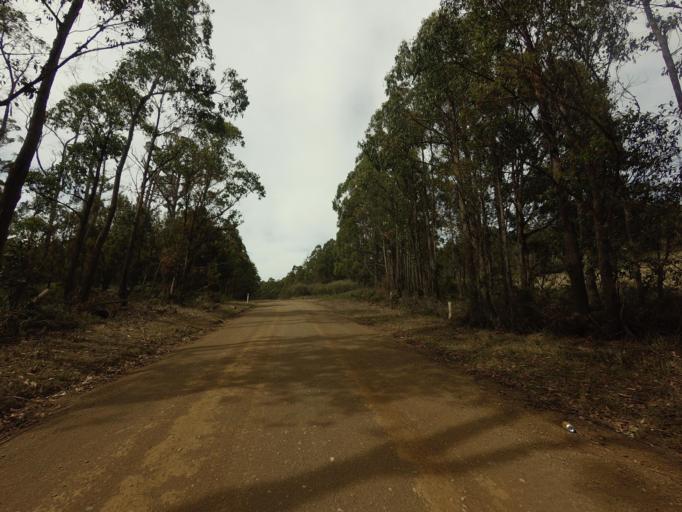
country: AU
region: Tasmania
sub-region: Sorell
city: Sorell
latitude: -42.4852
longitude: 147.6169
